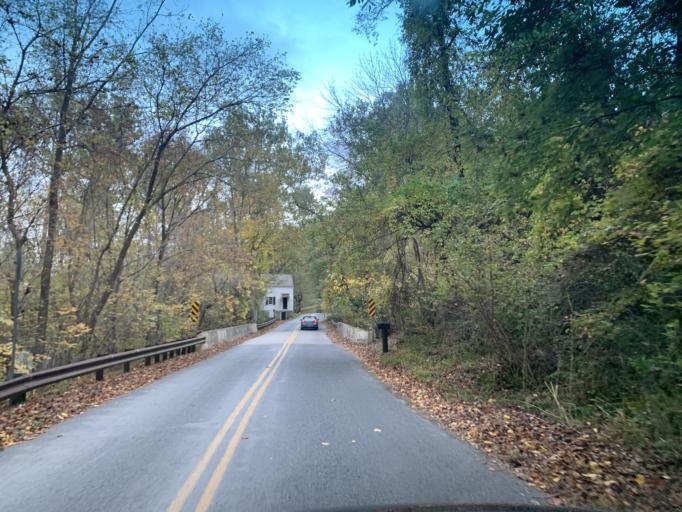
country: US
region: Maryland
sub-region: Harford County
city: Havre de Grace
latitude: 39.6092
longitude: -76.1442
